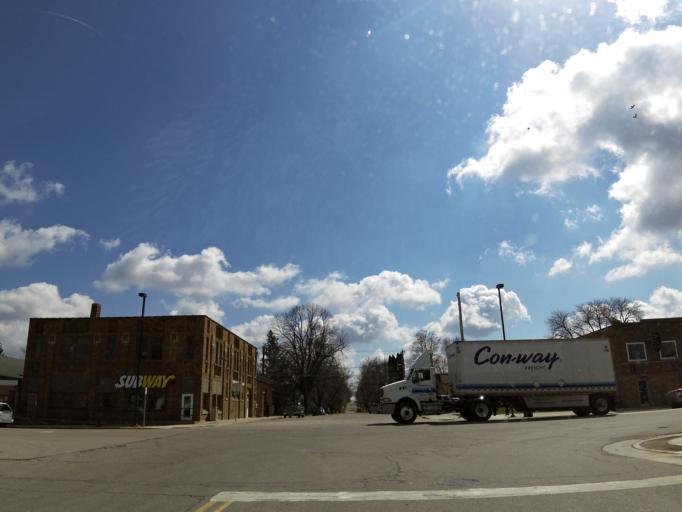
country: US
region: Minnesota
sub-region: Goodhue County
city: Kenyon
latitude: 44.2723
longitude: -92.9854
